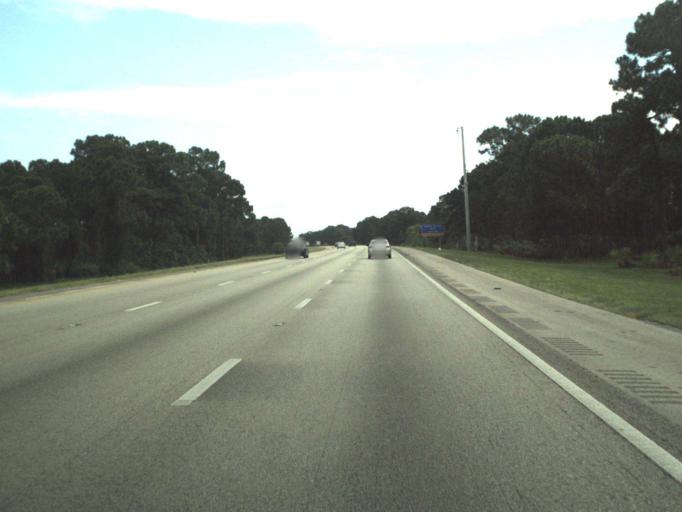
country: US
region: Florida
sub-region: Saint Lucie County
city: River Park
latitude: 27.3240
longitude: -80.4132
